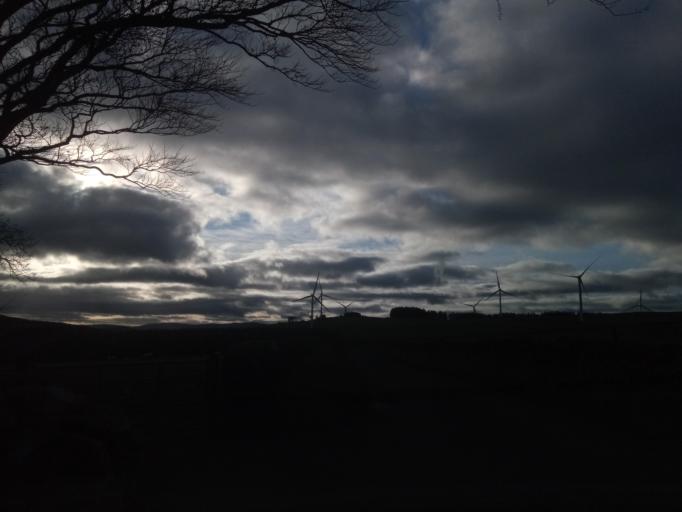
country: GB
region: Scotland
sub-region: The Scottish Borders
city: Galashiels
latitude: 55.6696
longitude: -2.8083
